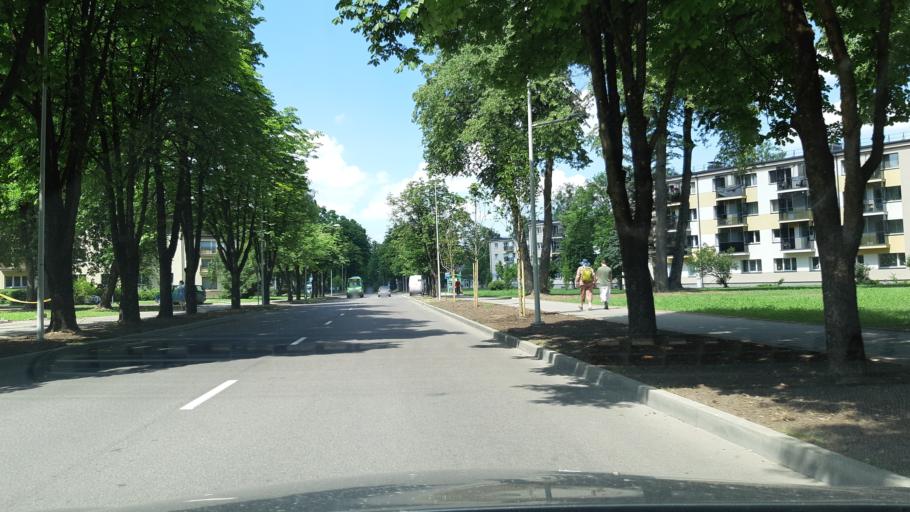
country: LT
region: Alytaus apskritis
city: Druskininkai
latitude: 54.0134
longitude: 23.9851
